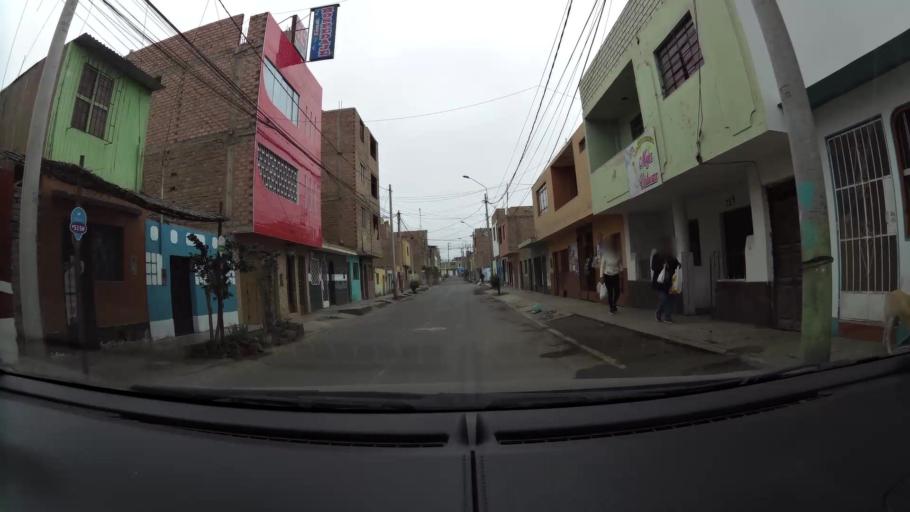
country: PE
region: Lima
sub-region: Barranca
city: Barranca
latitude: -10.7459
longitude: -77.7589
